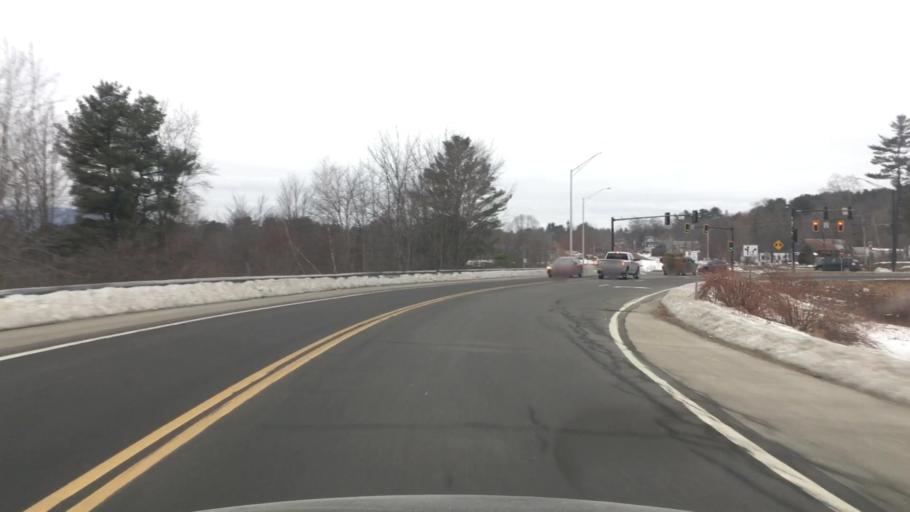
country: US
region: New Hampshire
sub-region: Merrimack County
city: Sutton
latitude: 43.2617
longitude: -71.9489
